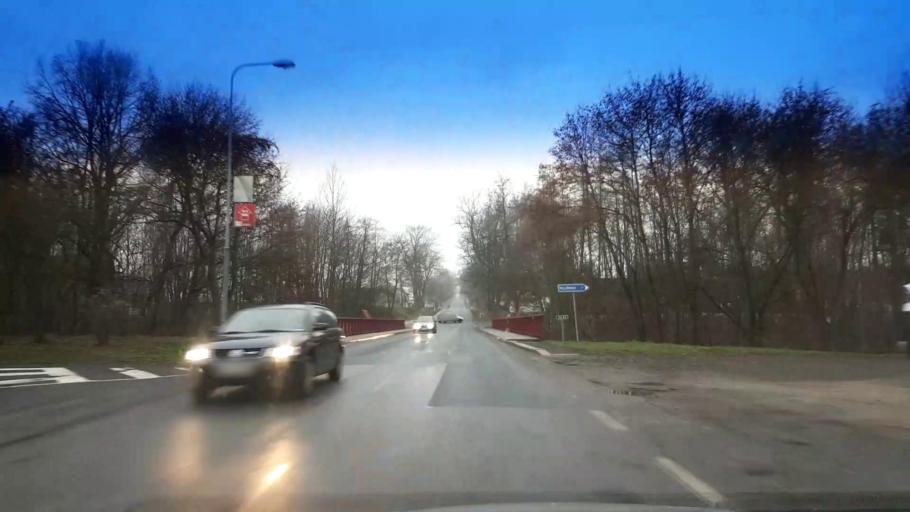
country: CZ
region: Karlovarsky
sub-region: Okres Cheb
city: Cheb
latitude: 50.0667
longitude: 12.3616
